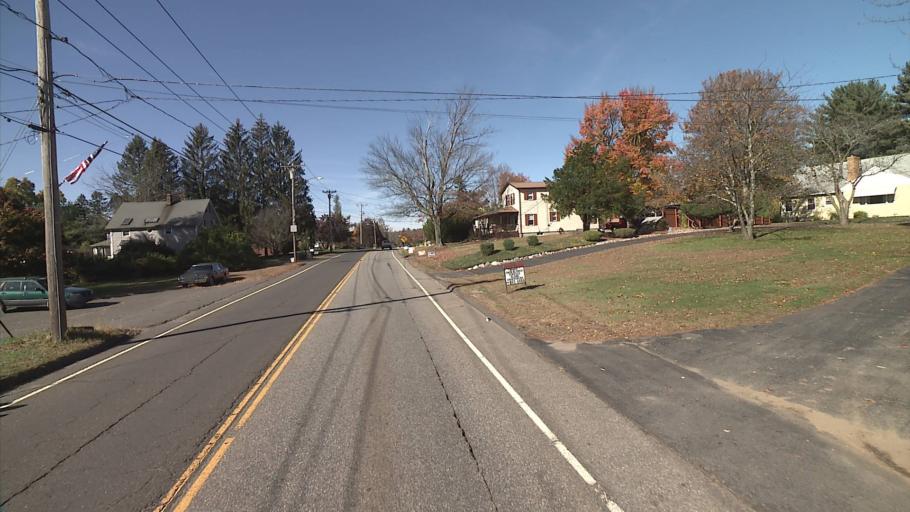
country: US
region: Connecticut
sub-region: Hartford County
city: Bristol
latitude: 41.6811
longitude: -72.9701
